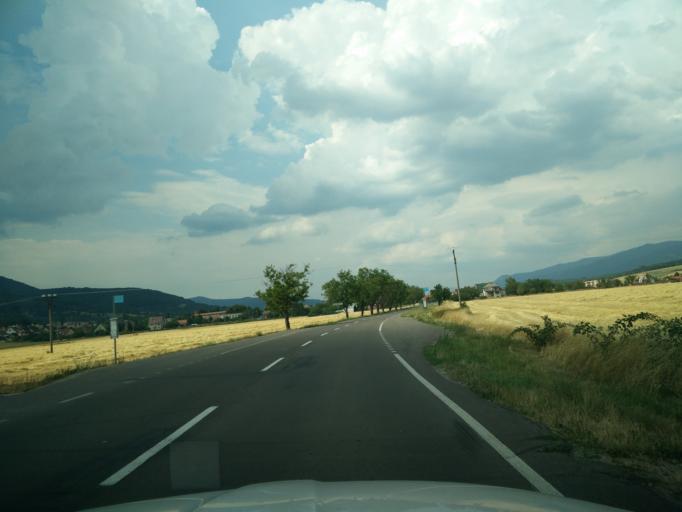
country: SK
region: Nitriansky
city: Novaky
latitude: 48.7593
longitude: 18.4969
